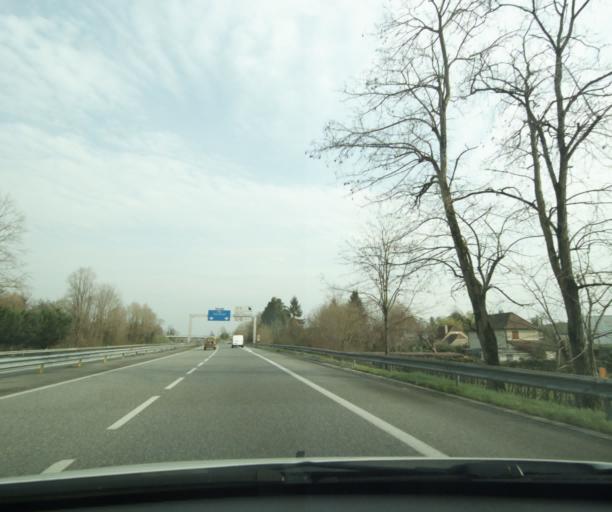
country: FR
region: Aquitaine
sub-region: Departement des Pyrenees-Atlantiques
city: Orthez
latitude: 43.4702
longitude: -0.7520
